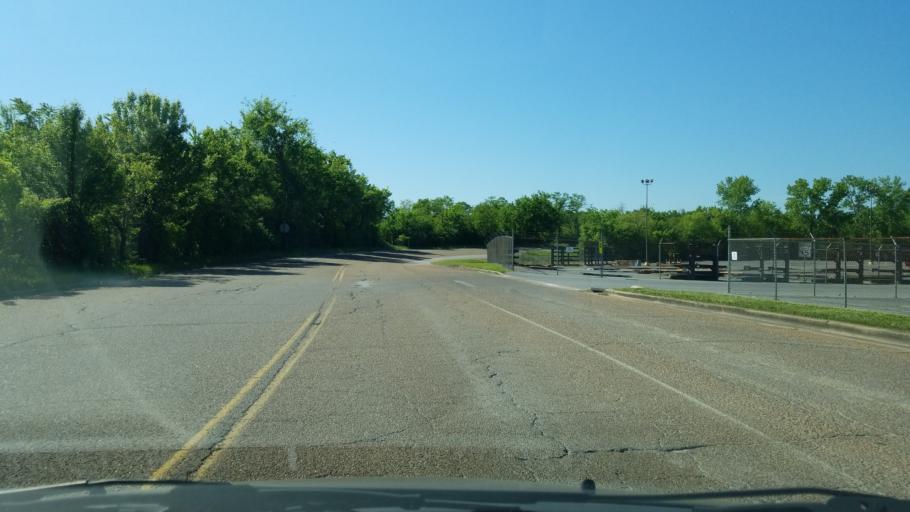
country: US
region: Tennessee
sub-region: Hamilton County
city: Chattanooga
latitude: 35.0583
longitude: -85.3247
